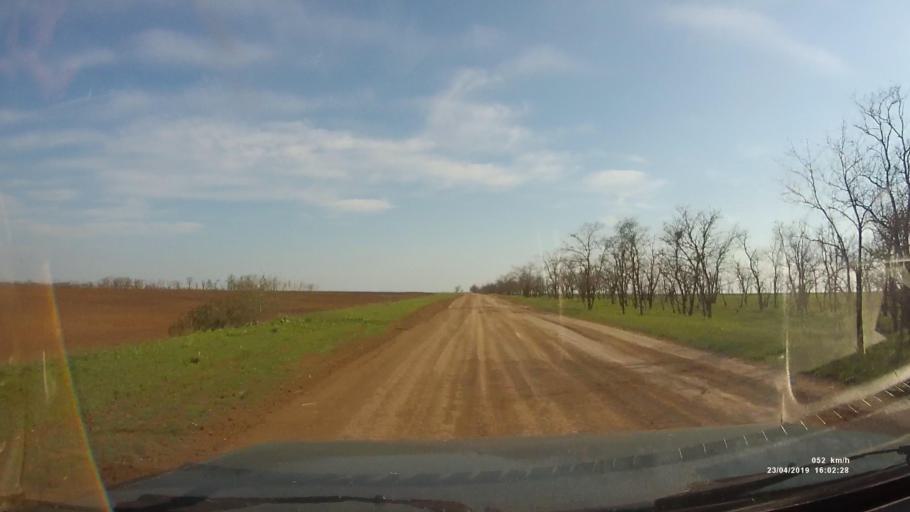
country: RU
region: Rostov
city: Remontnoye
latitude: 46.4941
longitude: 43.1070
